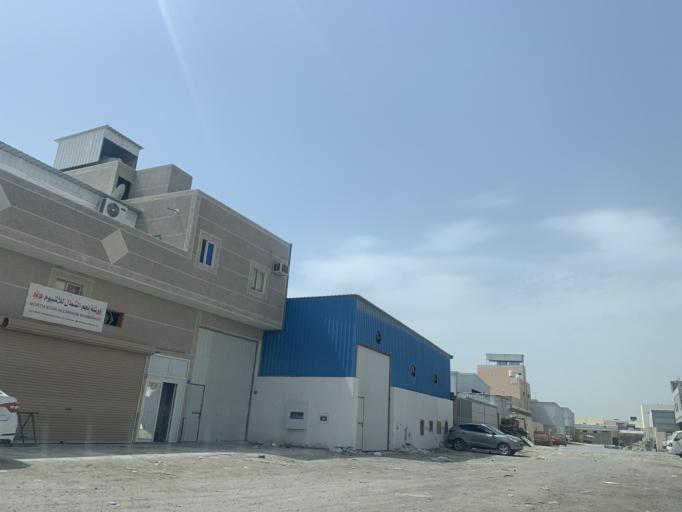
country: BH
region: Central Governorate
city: Madinat Hamad
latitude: 26.1412
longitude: 50.4866
